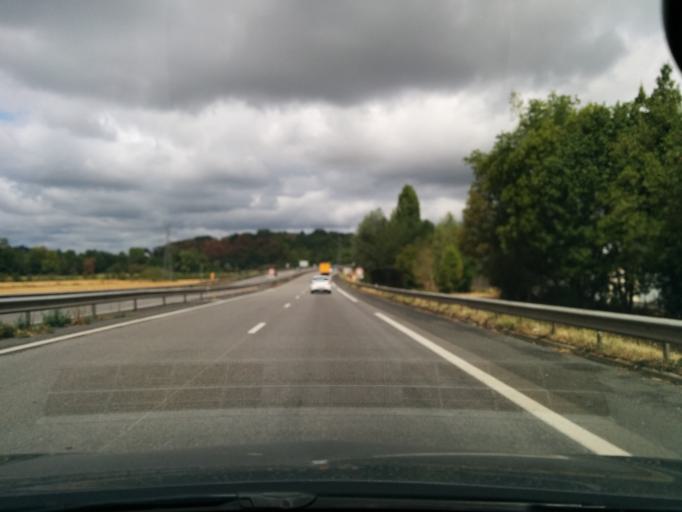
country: FR
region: Limousin
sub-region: Departement de la Correze
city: Saint-Pantaleon-de-Larche
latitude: 45.1589
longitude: 1.4812
